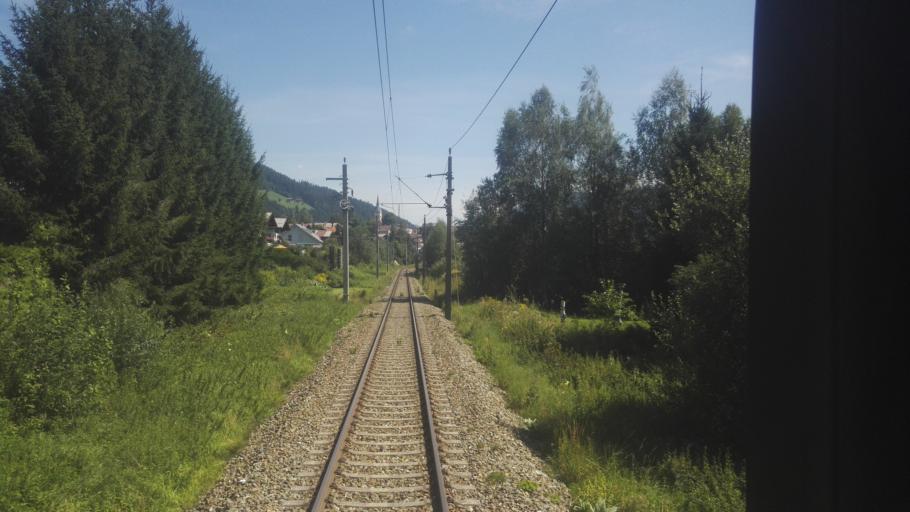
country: AT
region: Salzburg
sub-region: Politischer Bezirk Sankt Johann im Pongau
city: Radstadt
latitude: 47.3827
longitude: 13.4519
